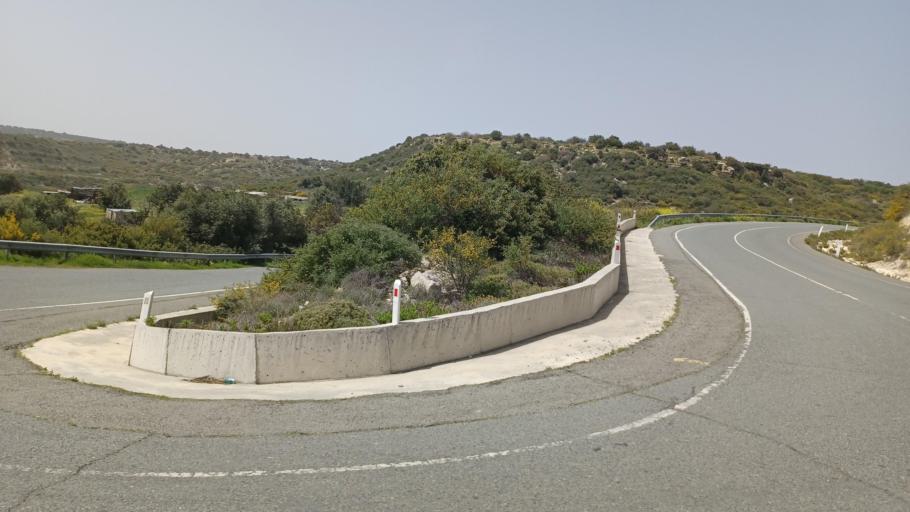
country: CY
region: Limassol
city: Pissouri
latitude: 34.7222
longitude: 32.7378
